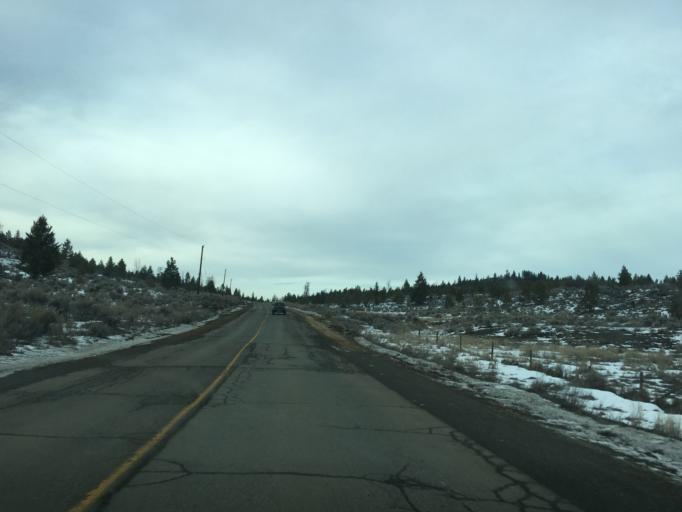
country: CA
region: British Columbia
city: Kamloops
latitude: 50.6324
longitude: -120.4448
